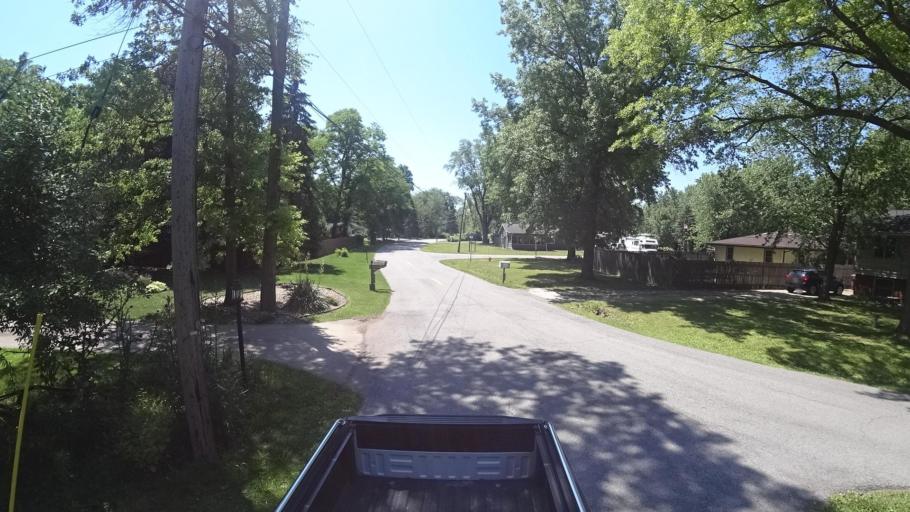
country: US
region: Indiana
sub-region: Porter County
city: Burns Harbor
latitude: 41.6150
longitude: -87.1267
